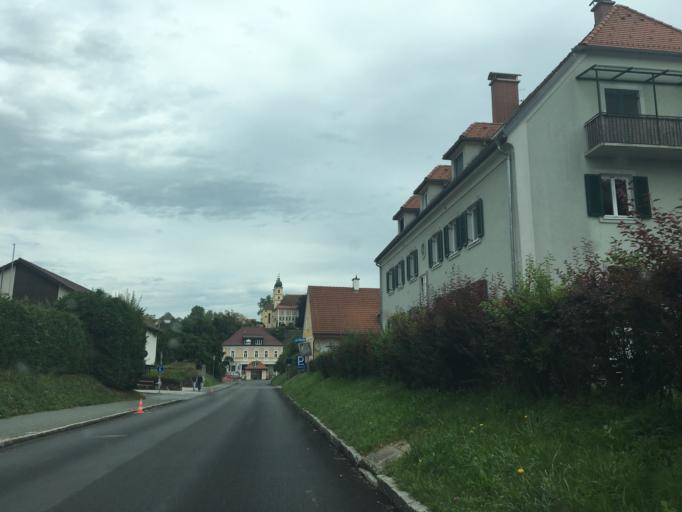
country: AT
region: Styria
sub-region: Politischer Bezirk Deutschlandsberg
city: Stainz
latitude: 46.8921
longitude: 15.2615
